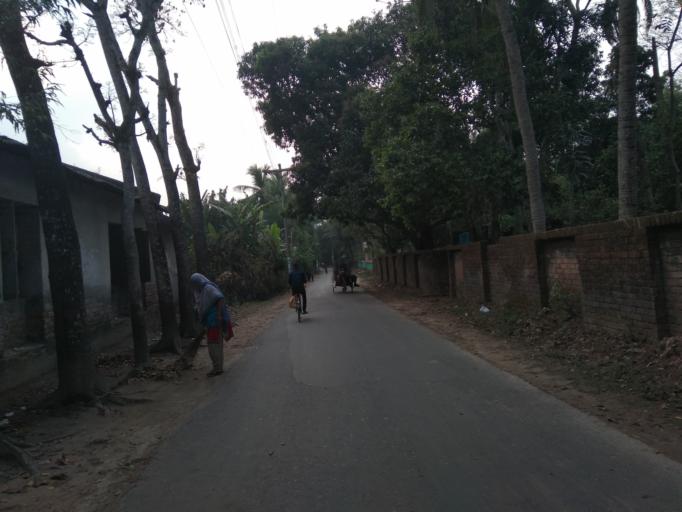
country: IN
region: West Bengal
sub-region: North 24 Parganas
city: Taki
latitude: 22.3427
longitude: 89.1159
